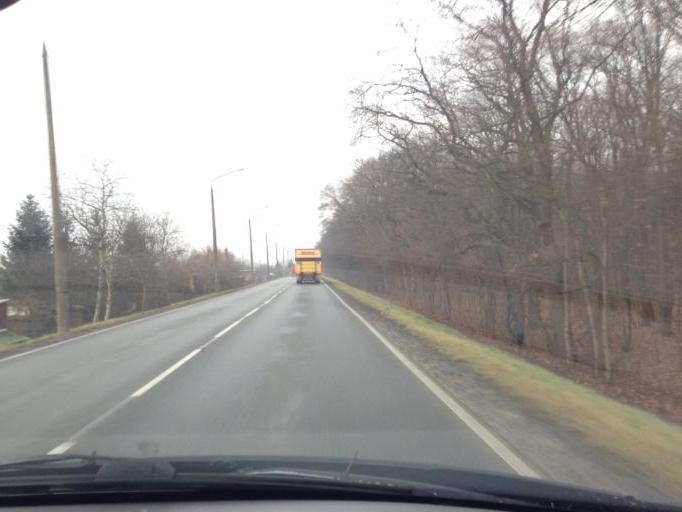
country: PL
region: Lesser Poland Voivodeship
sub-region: Powiat wielicki
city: Kokotow
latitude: 50.0531
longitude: 20.0609
